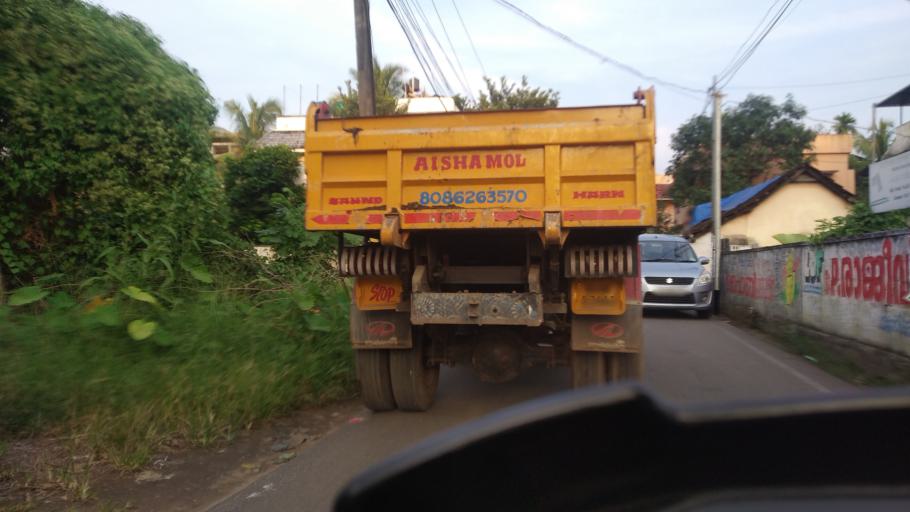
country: IN
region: Kerala
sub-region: Ernakulam
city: Elur
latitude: 10.0315
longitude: 76.3006
